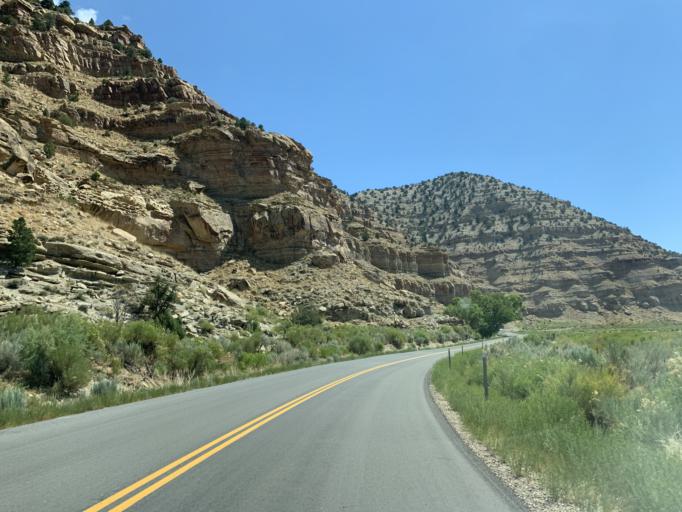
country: US
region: Utah
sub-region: Carbon County
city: East Carbon City
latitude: 39.8045
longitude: -110.3805
